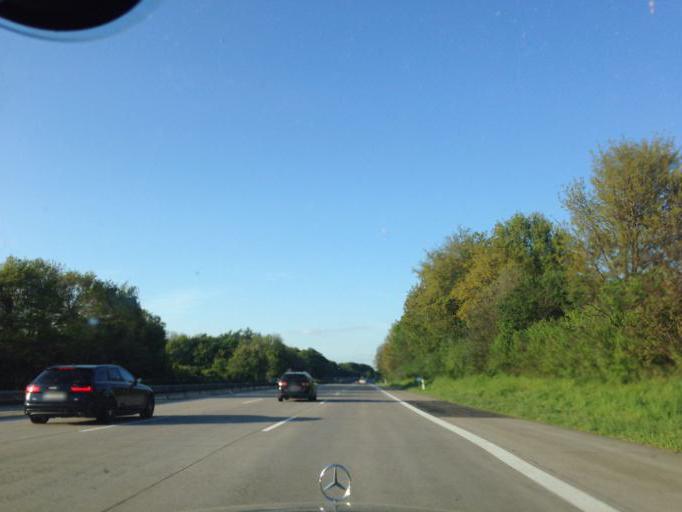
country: DE
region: Schleswig-Holstein
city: Lasbek
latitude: 53.7436
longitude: 10.3611
